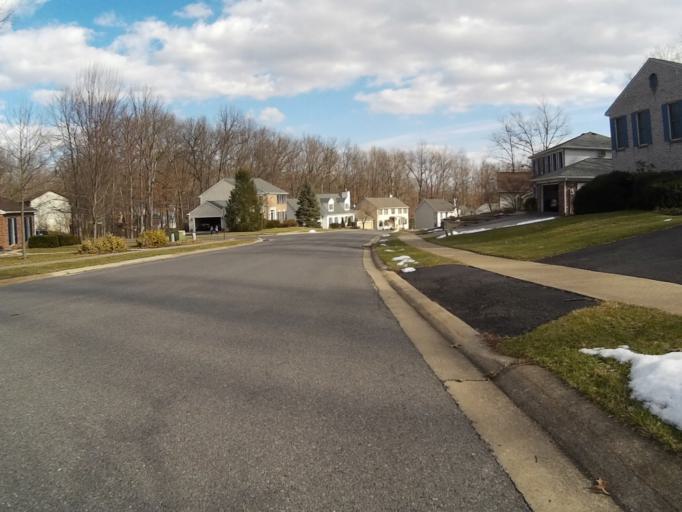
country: US
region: Pennsylvania
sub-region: Centre County
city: Park Forest Village
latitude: 40.7992
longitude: -77.9108
